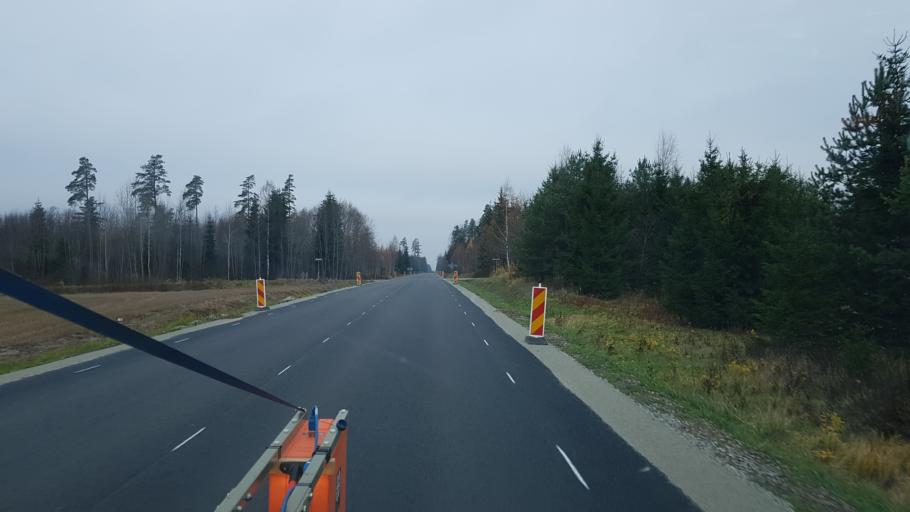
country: EE
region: Paernumaa
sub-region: Vaendra vald (alev)
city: Vandra
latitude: 58.8250
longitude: 25.1252
